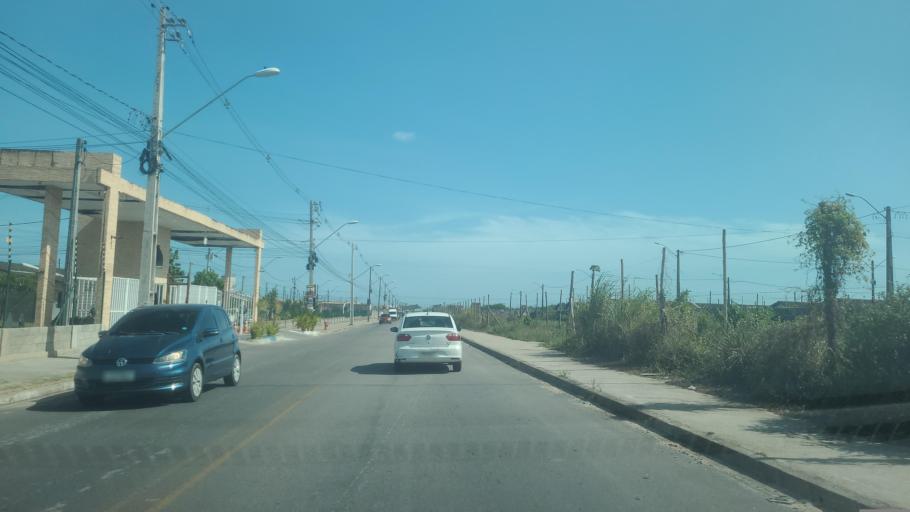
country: BR
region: Alagoas
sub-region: Satuba
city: Satuba
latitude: -9.5282
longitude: -35.7765
